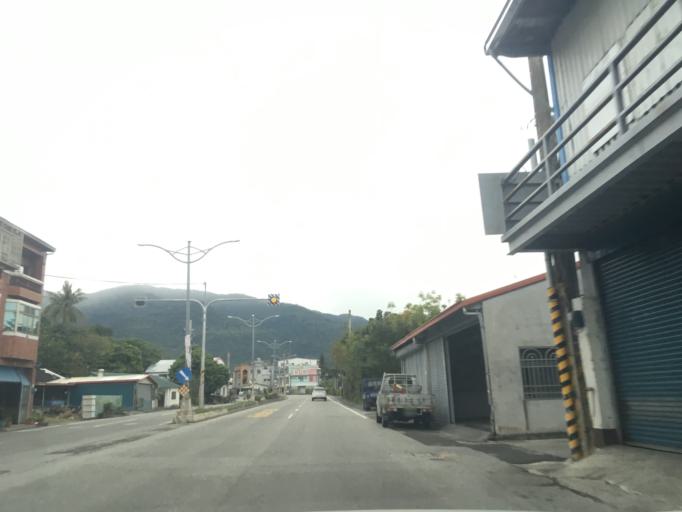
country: TW
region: Taiwan
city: Taitung City
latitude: 22.6932
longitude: 121.0461
